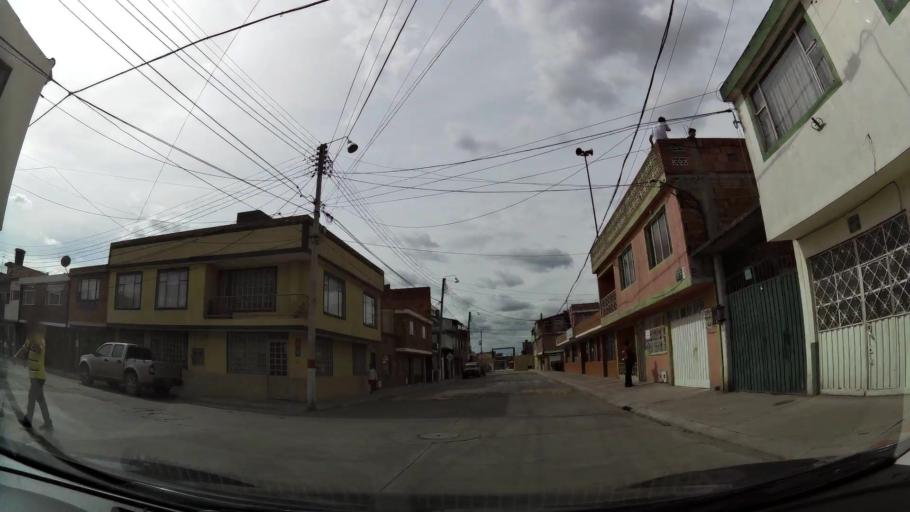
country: CO
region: Cundinamarca
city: Funza
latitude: 4.7098
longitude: -74.2029
